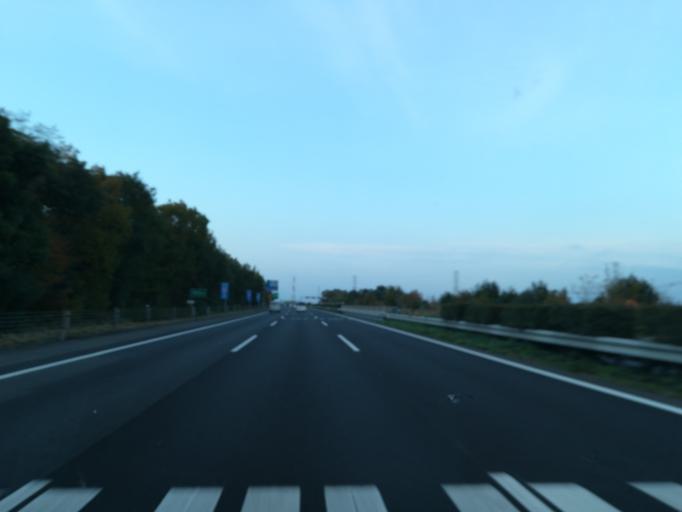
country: JP
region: Gunma
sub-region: Sawa-gun
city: Tamamura
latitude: 36.3001
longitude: 139.0954
